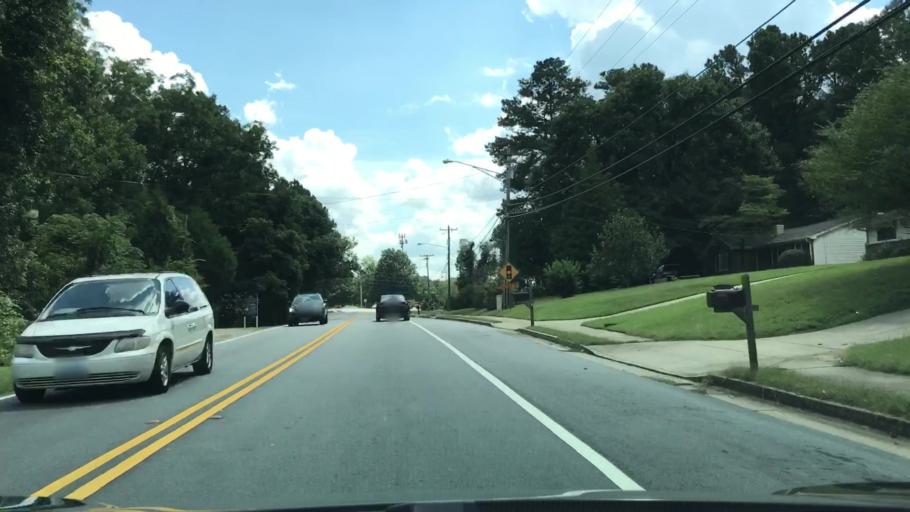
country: US
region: Georgia
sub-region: Gwinnett County
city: Snellville
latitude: 33.8902
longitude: -84.0640
